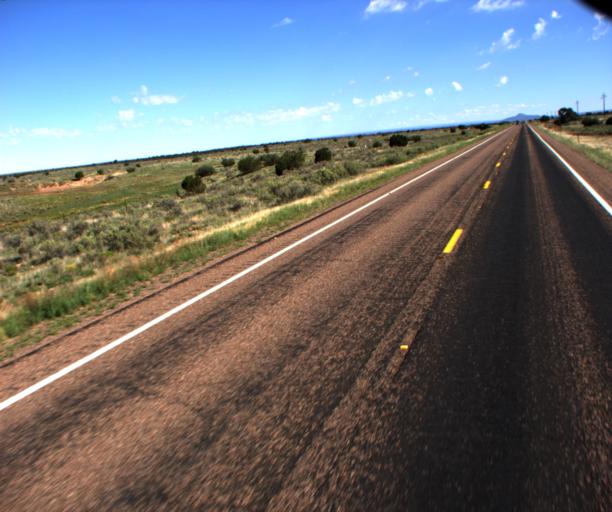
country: US
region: Arizona
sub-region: Coconino County
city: Williams
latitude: 35.5787
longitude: -112.1529
